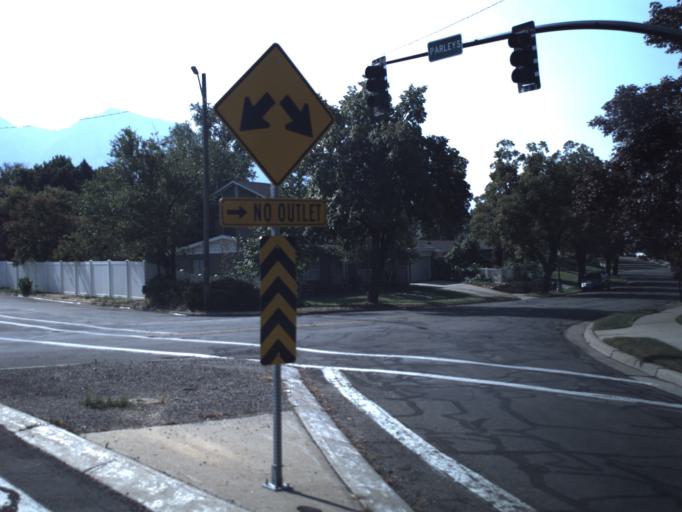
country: US
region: Utah
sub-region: Salt Lake County
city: Canyon Rim
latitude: 40.7187
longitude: -111.8141
